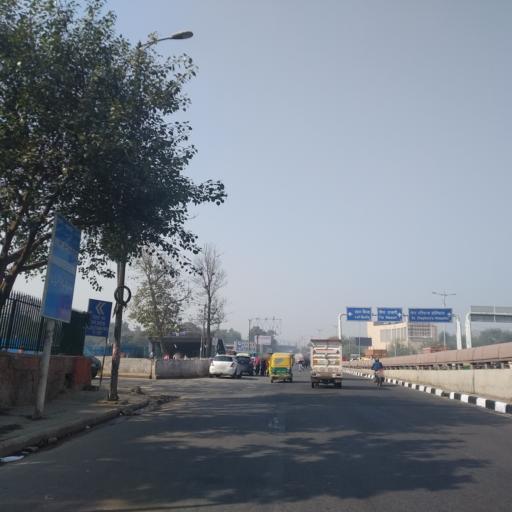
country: IN
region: NCT
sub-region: North Delhi
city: Delhi
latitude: 28.6692
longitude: 77.2292
